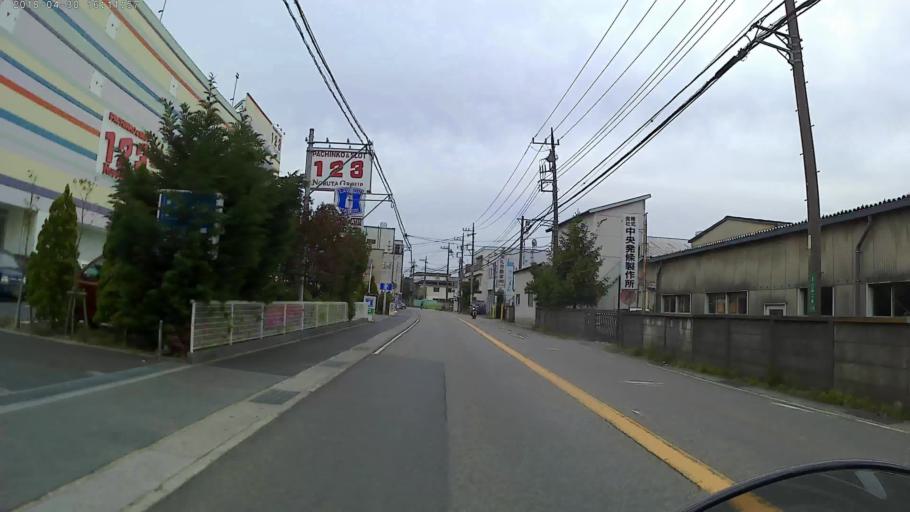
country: JP
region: Kanagawa
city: Minami-rinkan
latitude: 35.4993
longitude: 139.4279
